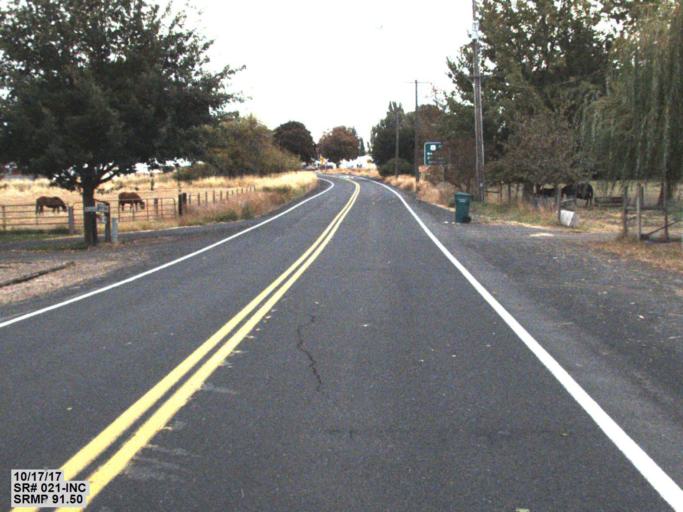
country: US
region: Washington
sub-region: Okanogan County
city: Coulee Dam
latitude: 47.7580
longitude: -118.7137
